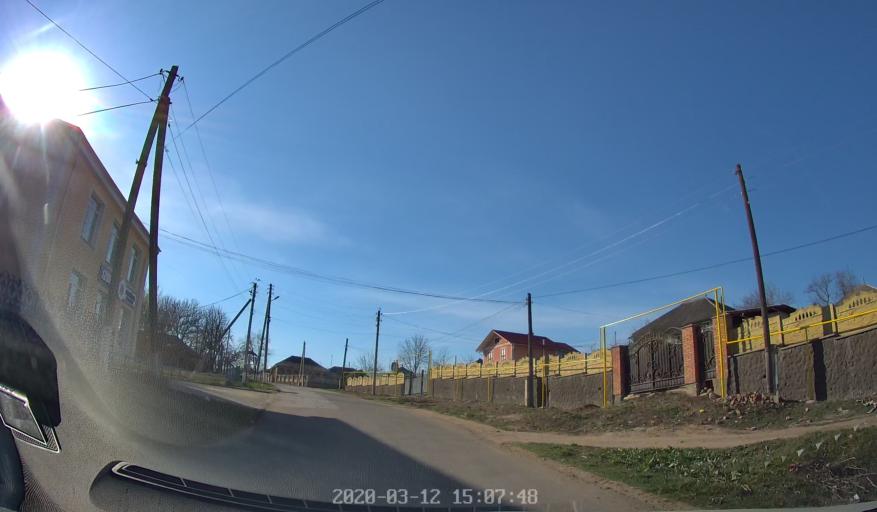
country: MD
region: Telenesti
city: Cocieri
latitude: 47.2212
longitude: 28.9985
